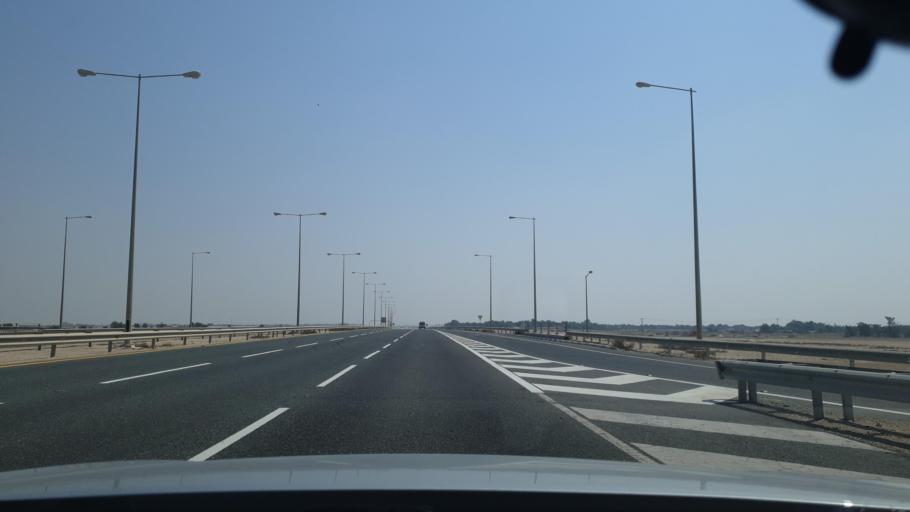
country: QA
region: Al Khawr
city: Al Khawr
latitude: 25.7868
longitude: 51.3949
